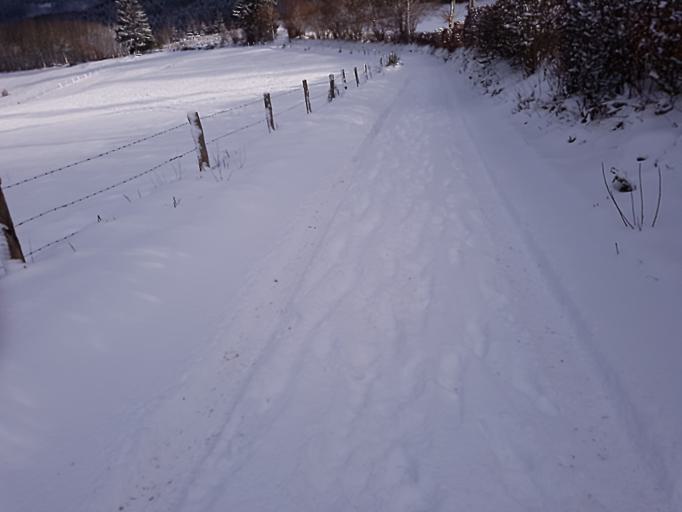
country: BE
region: Wallonia
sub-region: Province de Liege
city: Malmedy
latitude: 50.4381
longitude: 6.0528
